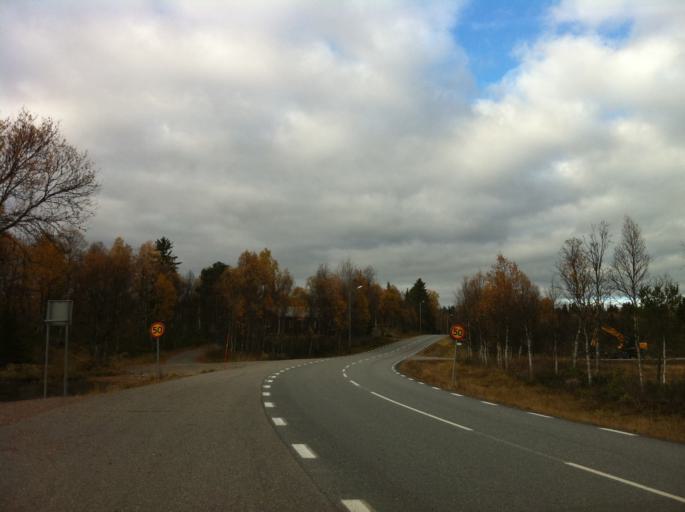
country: NO
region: Hedmark
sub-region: Engerdal
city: Engerdal
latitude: 62.0545
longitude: 12.3249
